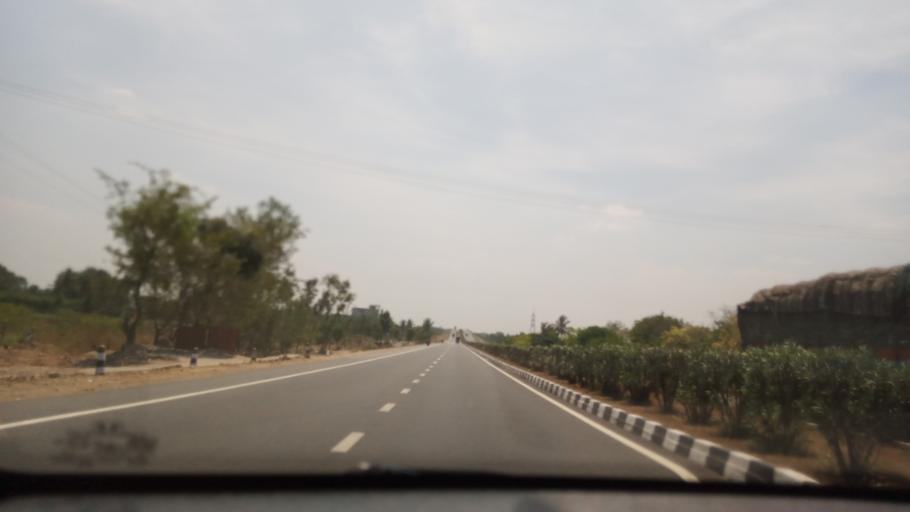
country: IN
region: Tamil Nadu
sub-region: Dharmapuri
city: Dharmapuri
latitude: 12.1568
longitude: 78.1527
